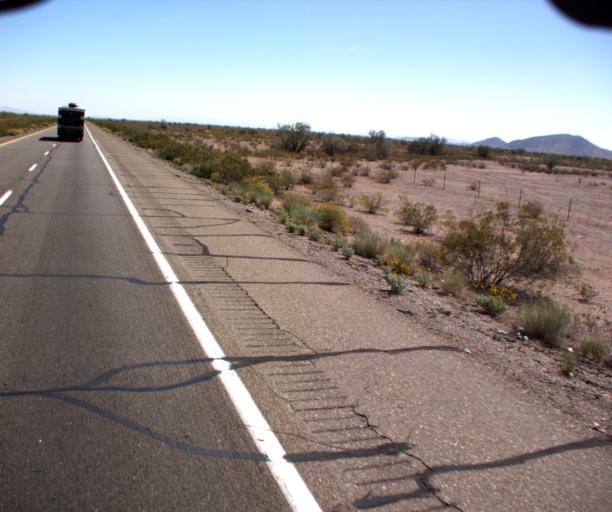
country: US
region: Arizona
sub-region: Maricopa County
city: Buckeye
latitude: 33.5063
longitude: -112.9870
